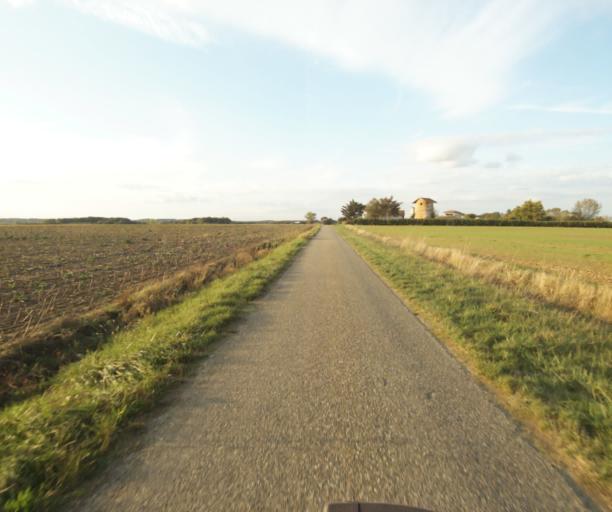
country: FR
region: Midi-Pyrenees
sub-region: Departement du Tarn-et-Garonne
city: Verdun-sur-Garonne
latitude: 43.8299
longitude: 1.1601
